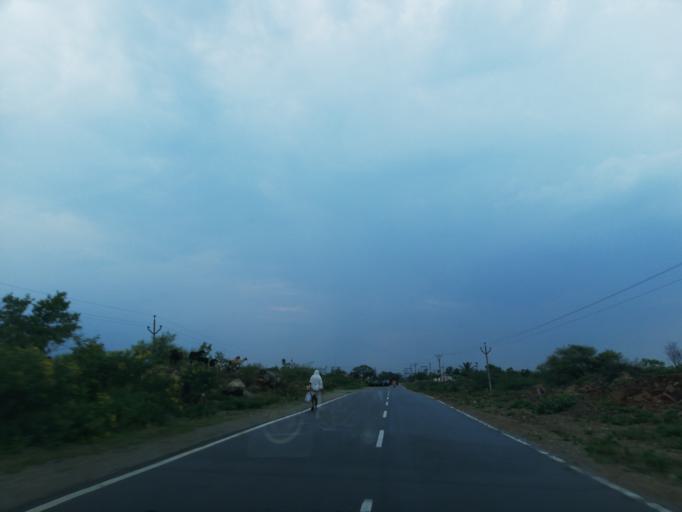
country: IN
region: Andhra Pradesh
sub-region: Guntur
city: Macherla
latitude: 16.6697
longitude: 79.2803
